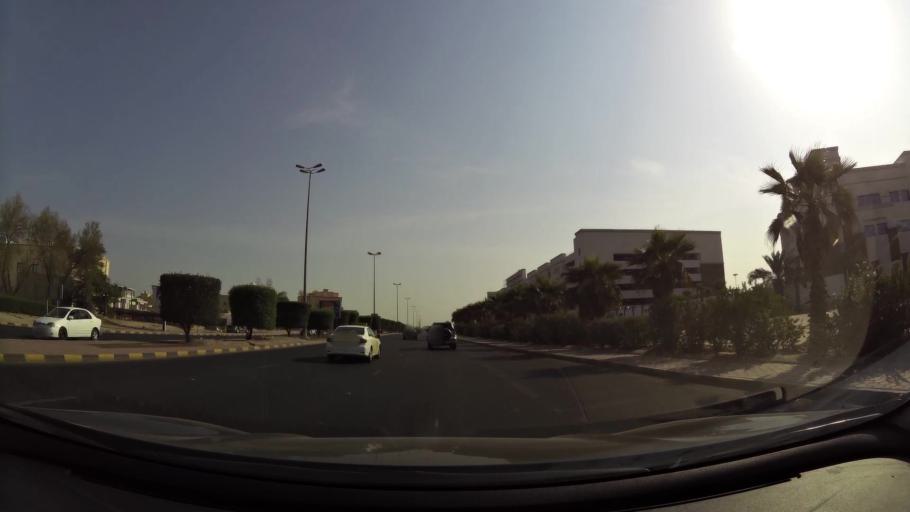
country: KW
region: Al Ahmadi
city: Al Fintas
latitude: 29.1677
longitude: 48.1010
